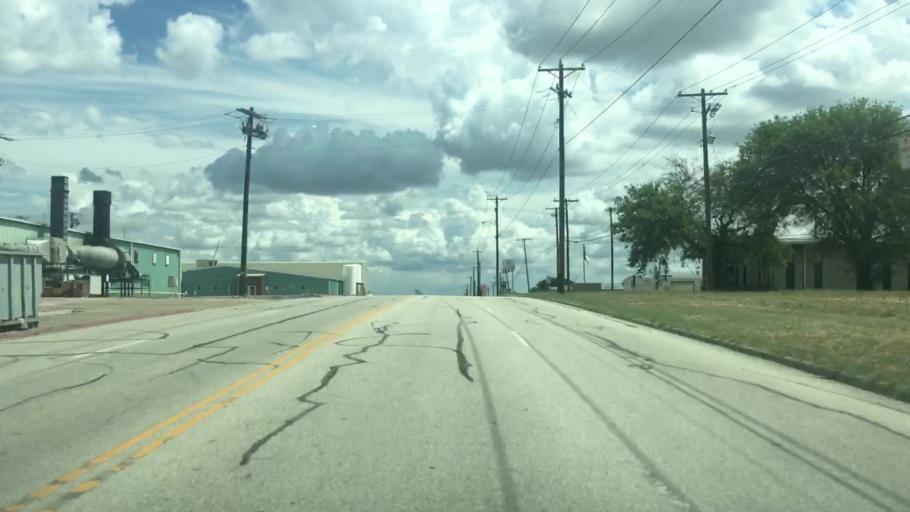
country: US
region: Texas
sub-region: Bell County
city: Temple
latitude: 31.1279
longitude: -97.3468
